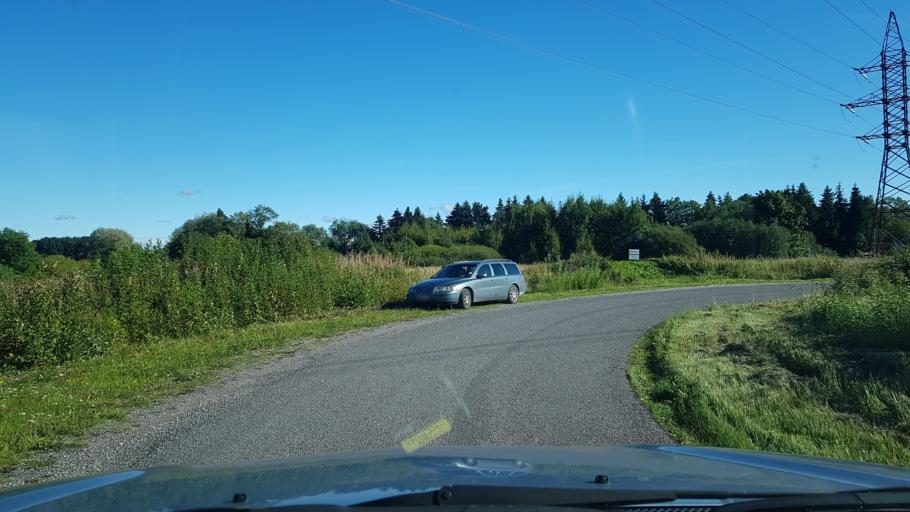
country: EE
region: Harju
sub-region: Joelaehtme vald
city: Loo
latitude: 59.4347
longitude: 24.9285
